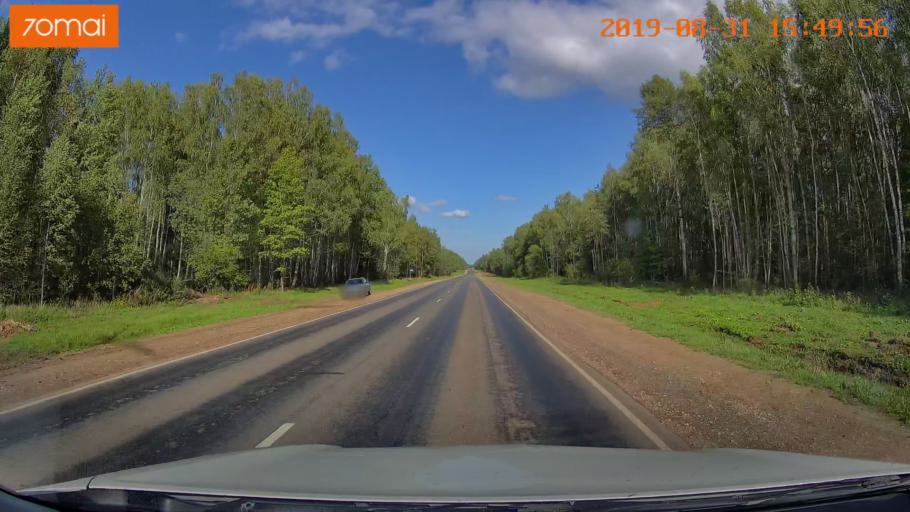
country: RU
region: Kaluga
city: Yukhnov
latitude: 54.6938
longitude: 35.0610
